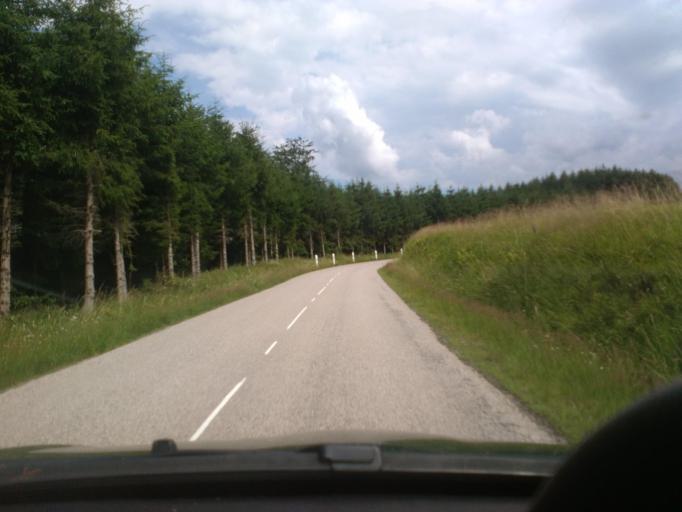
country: FR
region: Lorraine
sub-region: Departement des Vosges
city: Senones
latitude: 48.3976
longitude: 7.0280
